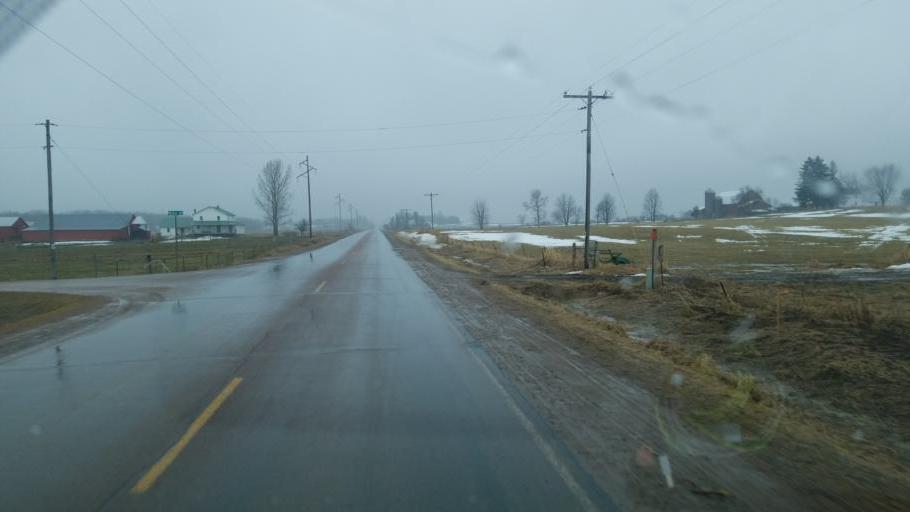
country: US
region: Wisconsin
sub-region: Clark County
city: Neillsville
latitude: 44.5468
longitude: -90.3962
